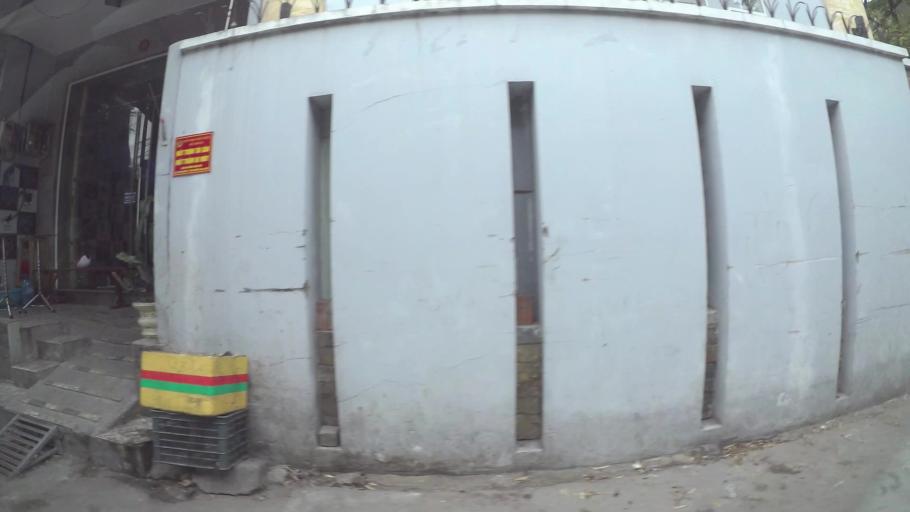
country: VN
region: Da Nang
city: Thanh Khe
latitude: 16.0677
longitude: 108.1942
